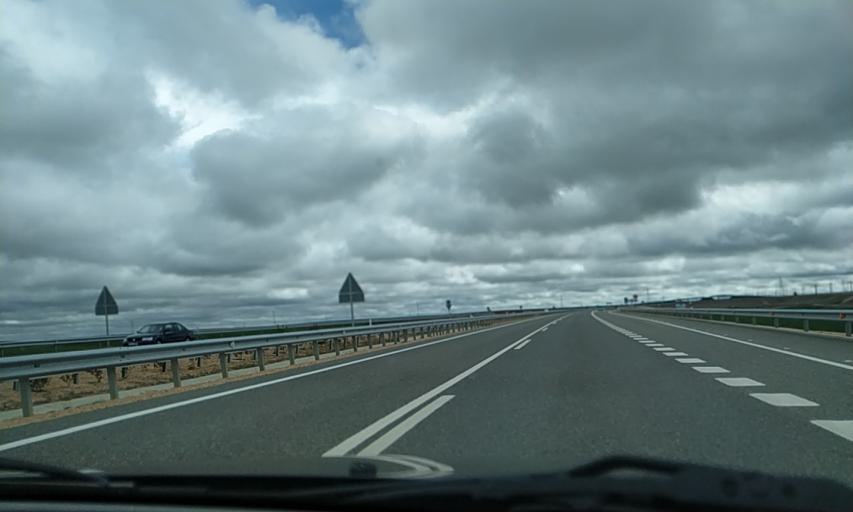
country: ES
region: Castille and Leon
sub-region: Provincia de Zamora
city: Montamarta
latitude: 41.6376
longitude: -5.7911
